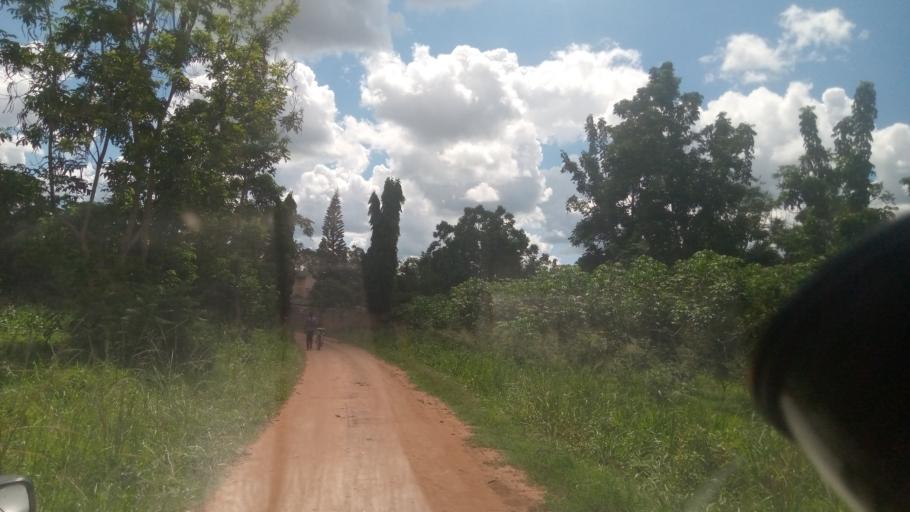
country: UG
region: Northern Region
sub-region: Lira District
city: Lira
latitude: 2.2431
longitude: 32.9042
